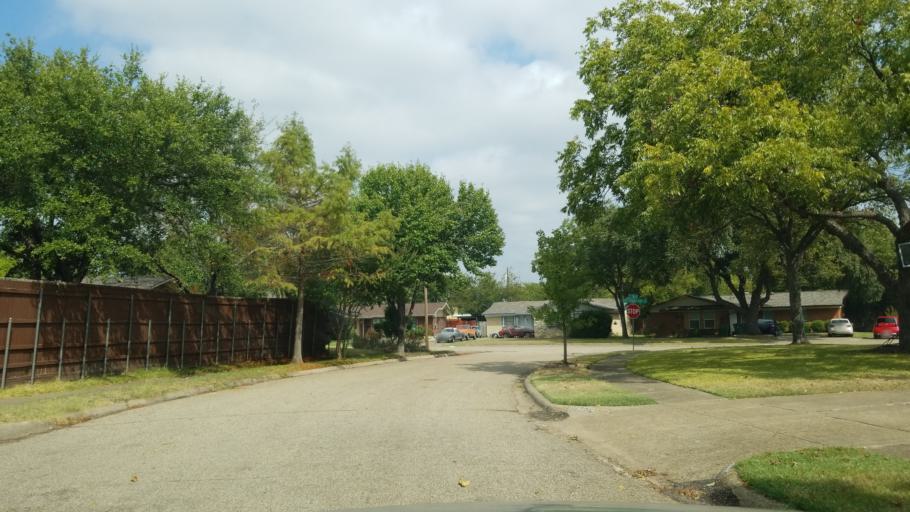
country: US
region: Texas
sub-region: Dallas County
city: Garland
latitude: 32.8923
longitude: -96.6638
